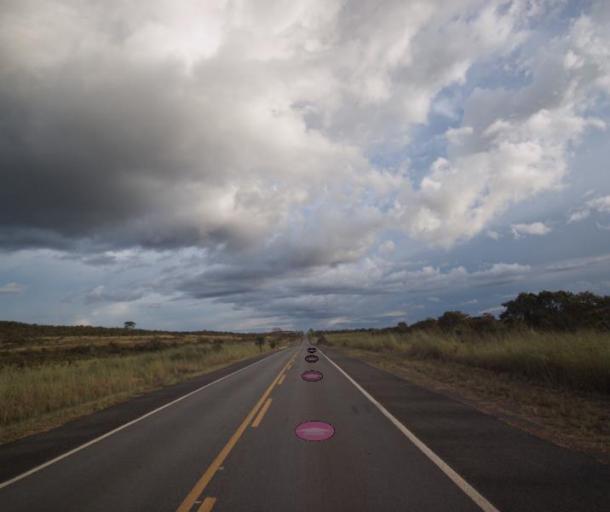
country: BR
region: Goias
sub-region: Barro Alto
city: Barro Alto
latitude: -14.8586
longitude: -48.6393
